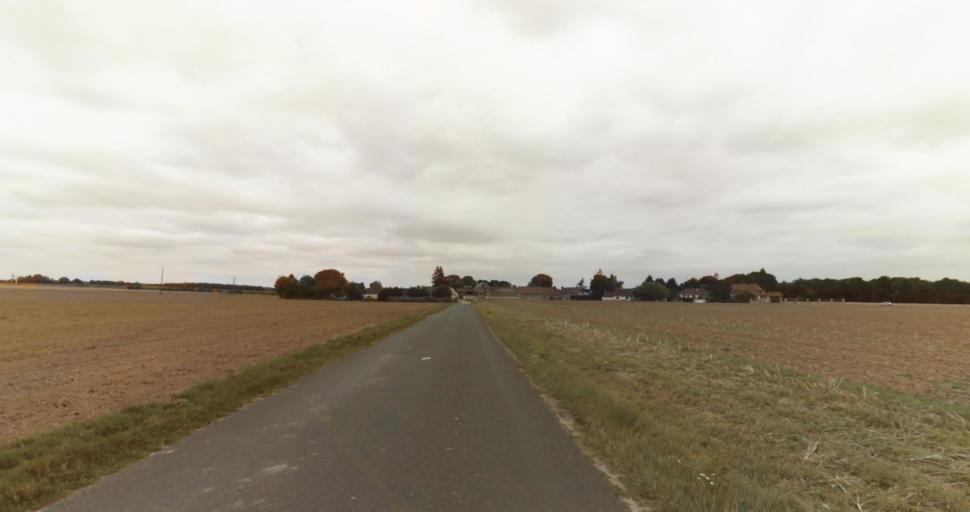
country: FR
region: Haute-Normandie
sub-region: Departement de l'Eure
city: Evreux
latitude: 49.0033
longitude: 1.2008
